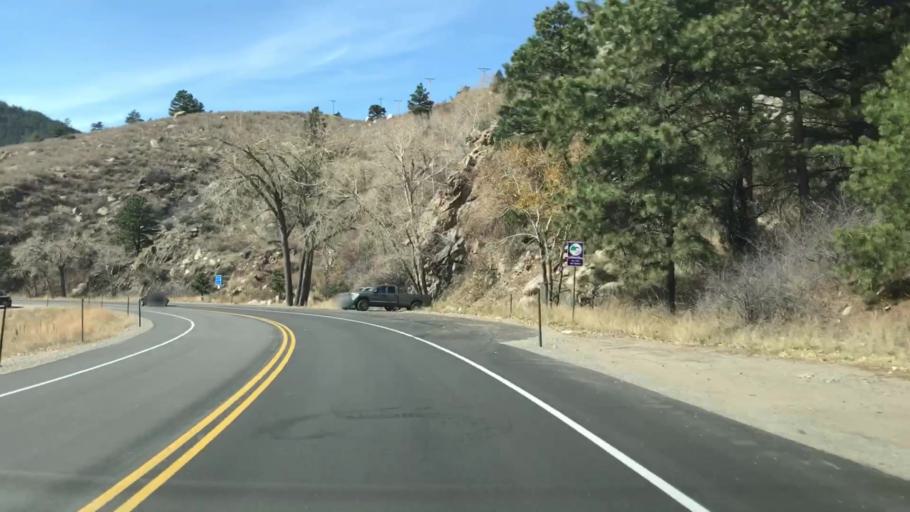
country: US
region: Colorado
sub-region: Boulder County
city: Lyons
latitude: 40.4298
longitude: -105.3149
